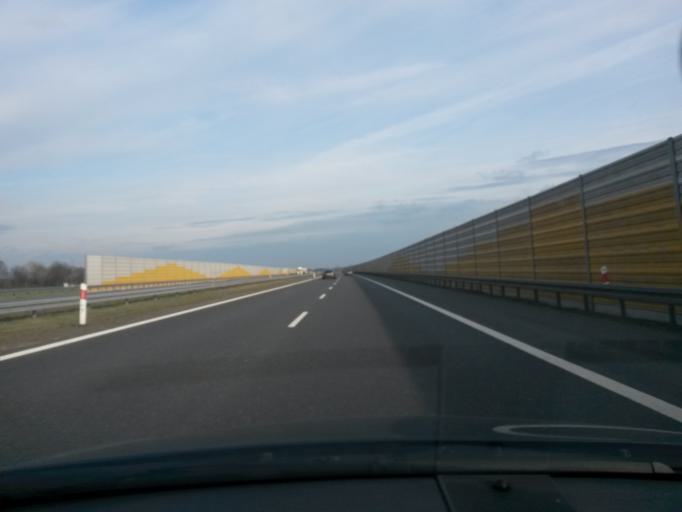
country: PL
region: Lodz Voivodeship
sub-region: Powiat poddebicki
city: Wartkowice
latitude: 52.0025
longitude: 18.9940
